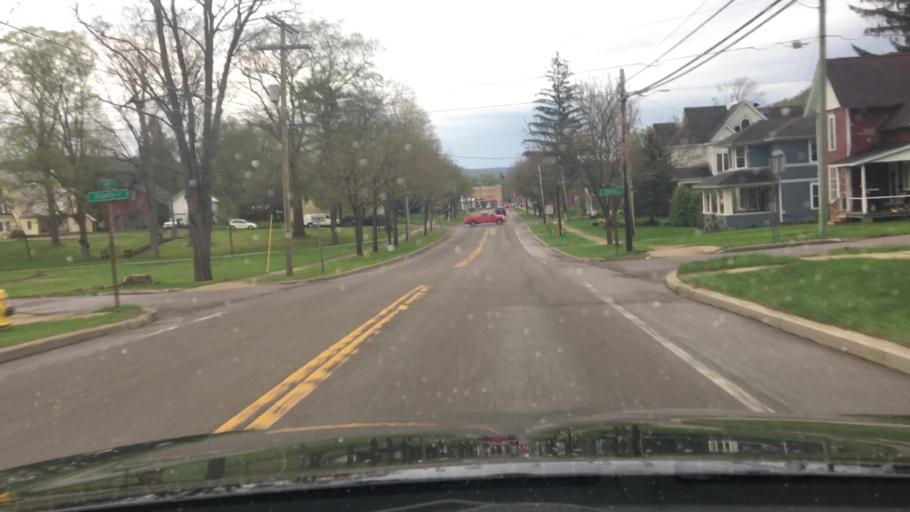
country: US
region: New York
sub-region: Cattaraugus County
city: Little Valley
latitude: 42.2514
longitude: -78.8025
